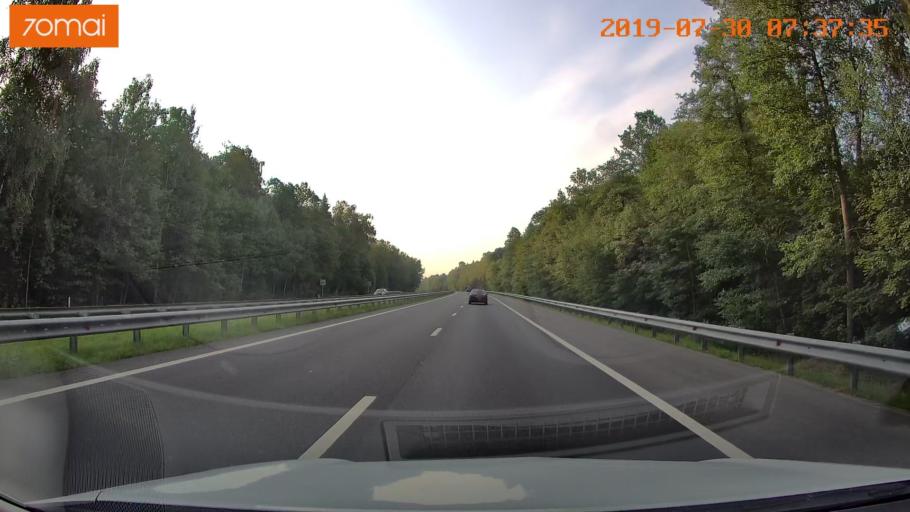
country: RU
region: Kaliningrad
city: Gvardeysk
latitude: 54.6549
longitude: 21.1484
